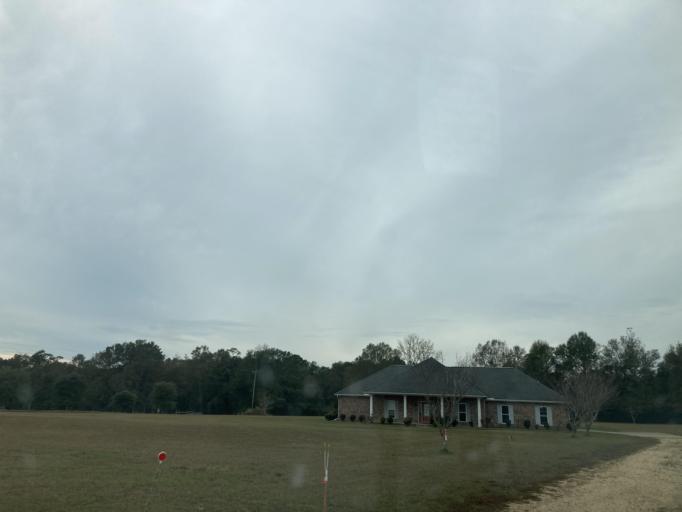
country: US
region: Mississippi
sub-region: Lamar County
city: Purvis
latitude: 31.0877
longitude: -89.4321
